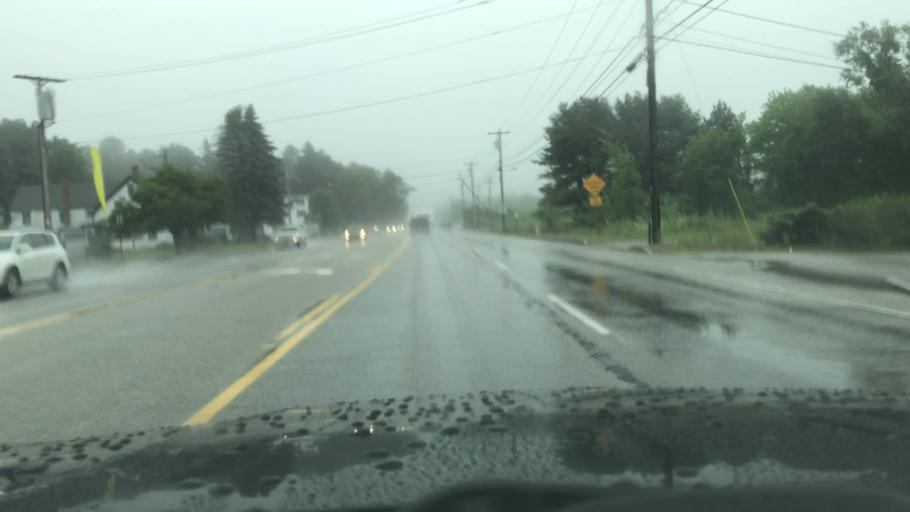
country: US
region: Maine
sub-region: Cumberland County
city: West Scarborough
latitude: 43.5518
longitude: -70.4071
